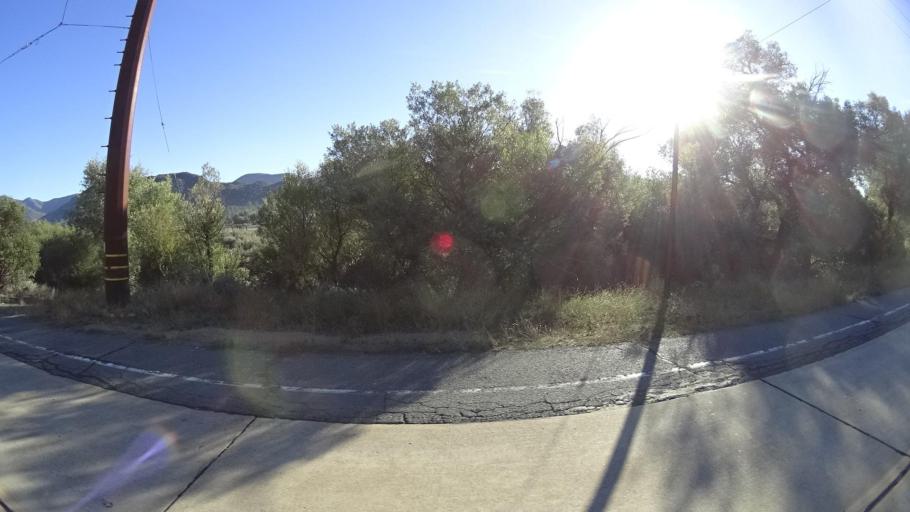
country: US
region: California
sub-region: San Diego County
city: Pine Valley
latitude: 32.8328
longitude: -116.5332
